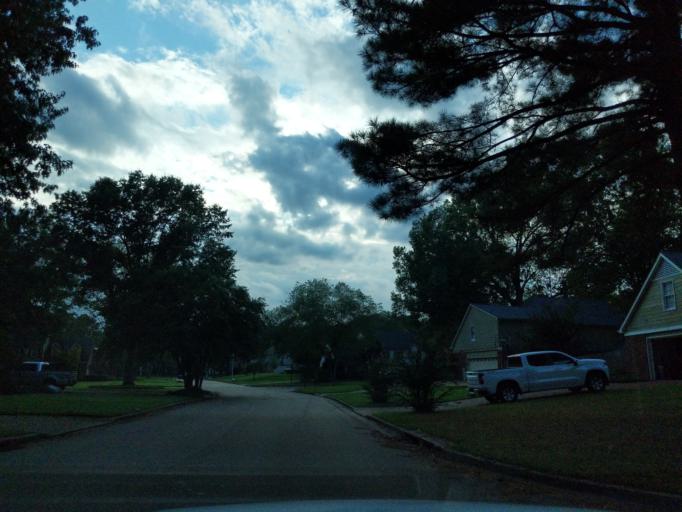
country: US
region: Tennessee
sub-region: Shelby County
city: Germantown
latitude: 35.0668
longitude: -89.7837
